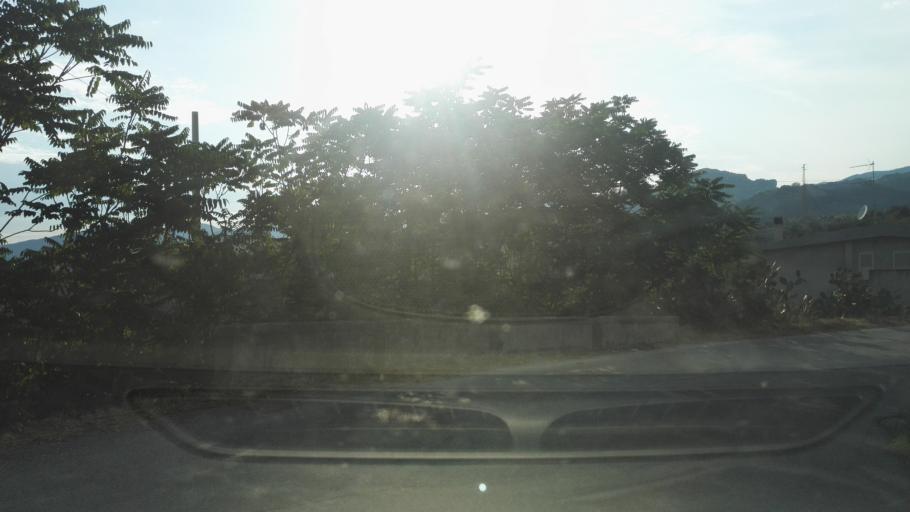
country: IT
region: Calabria
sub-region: Provincia di Reggio Calabria
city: Stignano
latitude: 38.4083
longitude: 16.4722
